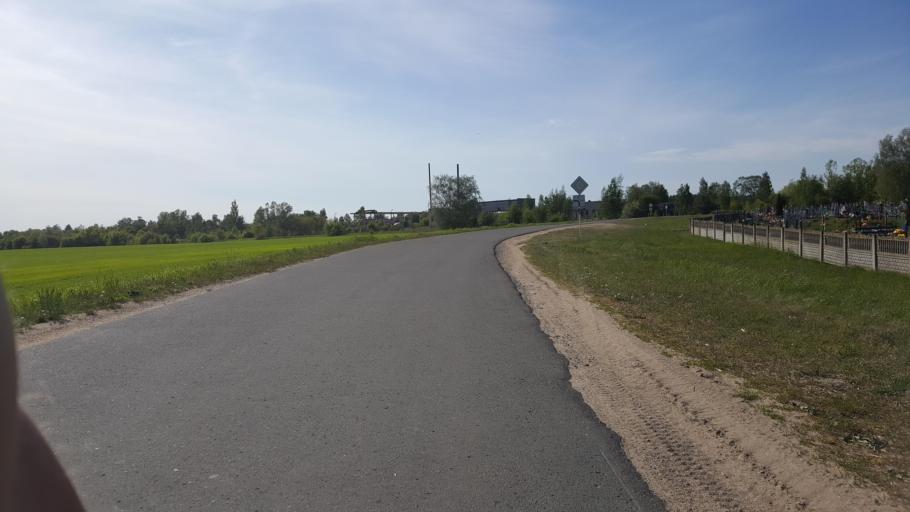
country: BY
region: Brest
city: Zhabinka
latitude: 52.3200
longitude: 23.9438
